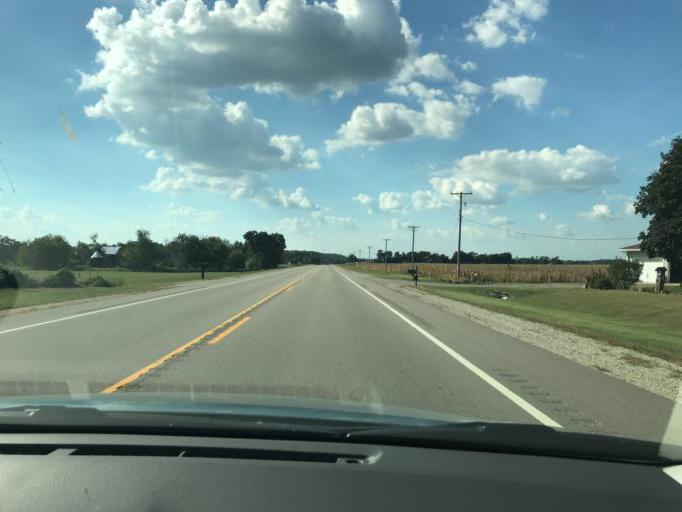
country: US
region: Wisconsin
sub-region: Green County
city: Brodhead
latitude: 42.5857
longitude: -89.3858
